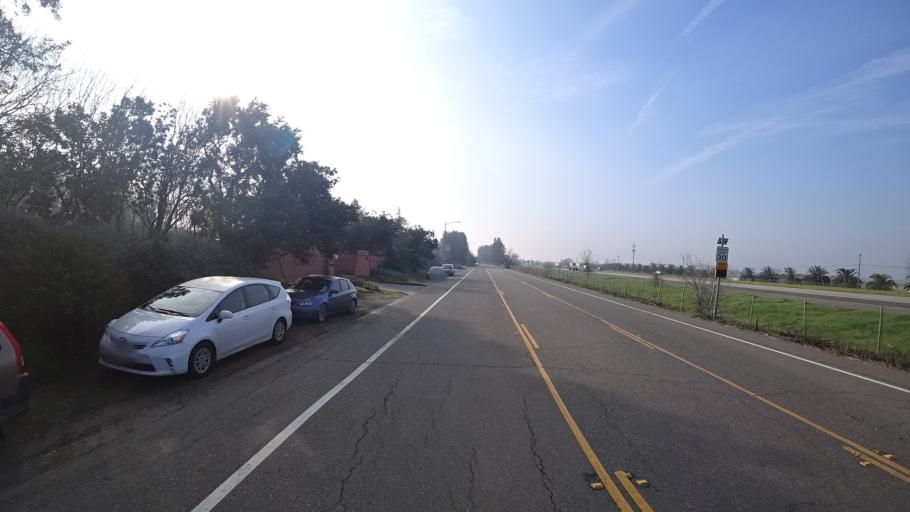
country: US
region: California
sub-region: Yolo County
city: Davis
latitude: 38.5712
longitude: -121.7672
